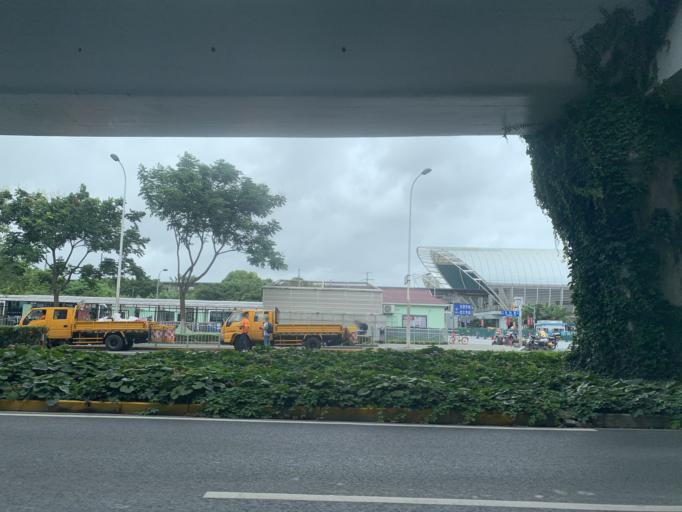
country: CN
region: Shanghai Shi
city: Huamu
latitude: 31.2056
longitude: 121.5553
